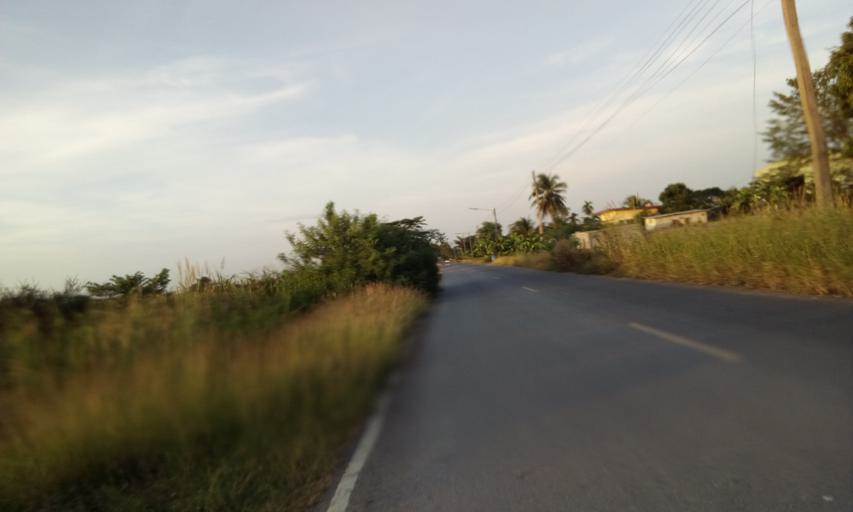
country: TH
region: Pathum Thani
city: Nong Suea
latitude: 14.0436
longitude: 100.8667
